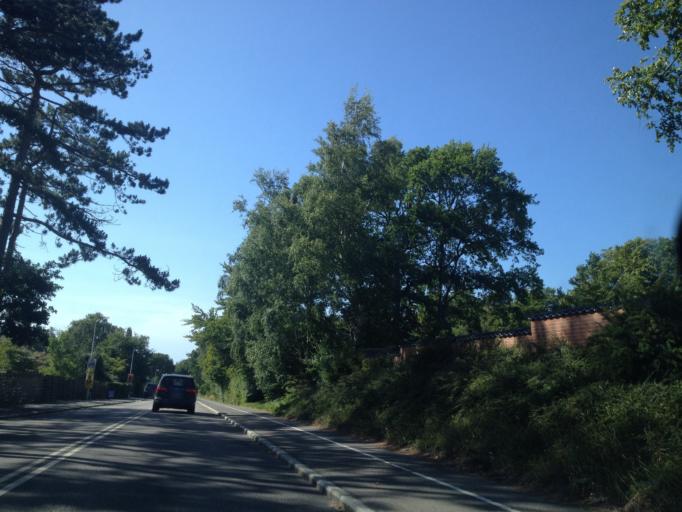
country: DK
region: Capital Region
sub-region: Gribskov Kommune
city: Helsinge
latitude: 56.0962
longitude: 12.1703
